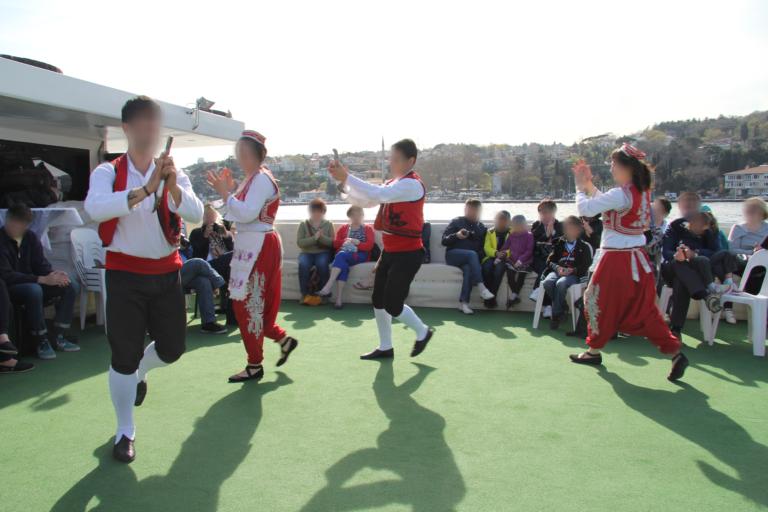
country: TR
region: Istanbul
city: Sisli
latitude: 41.1200
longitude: 29.0722
